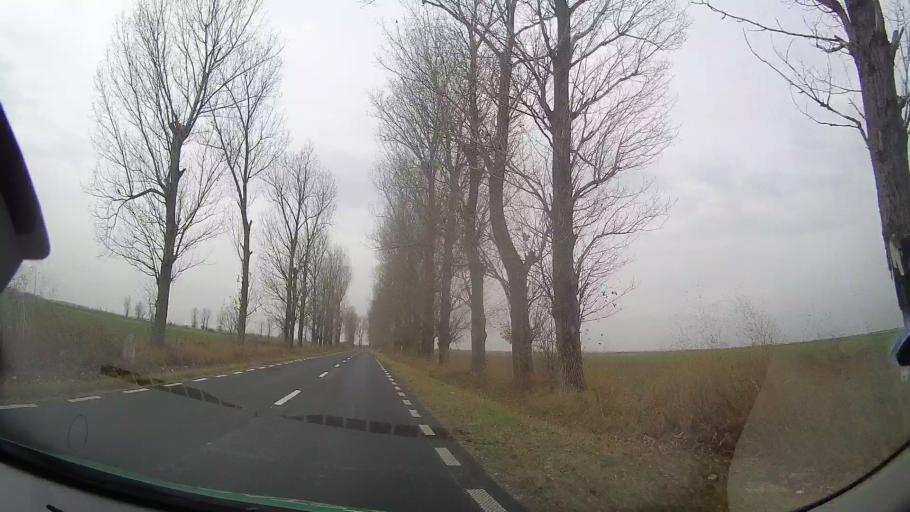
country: RO
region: Ilfov
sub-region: Comuna Gruiu
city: Lipia
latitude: 44.7230
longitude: 26.2769
